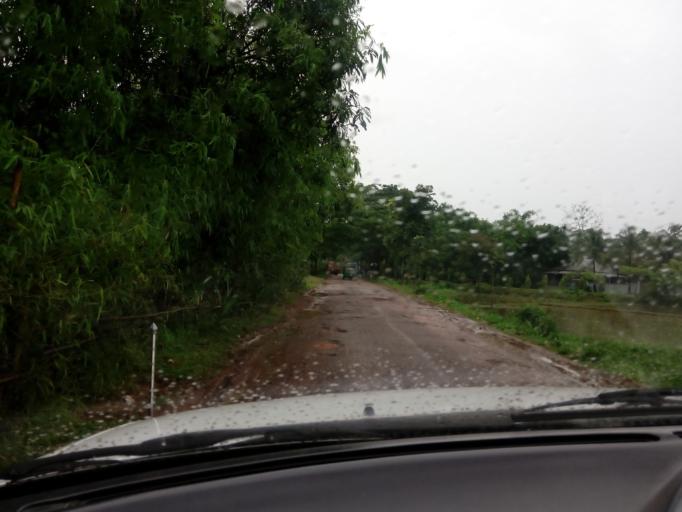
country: BD
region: Sylhet
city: Sylhet
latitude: 24.9662
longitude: 91.7926
